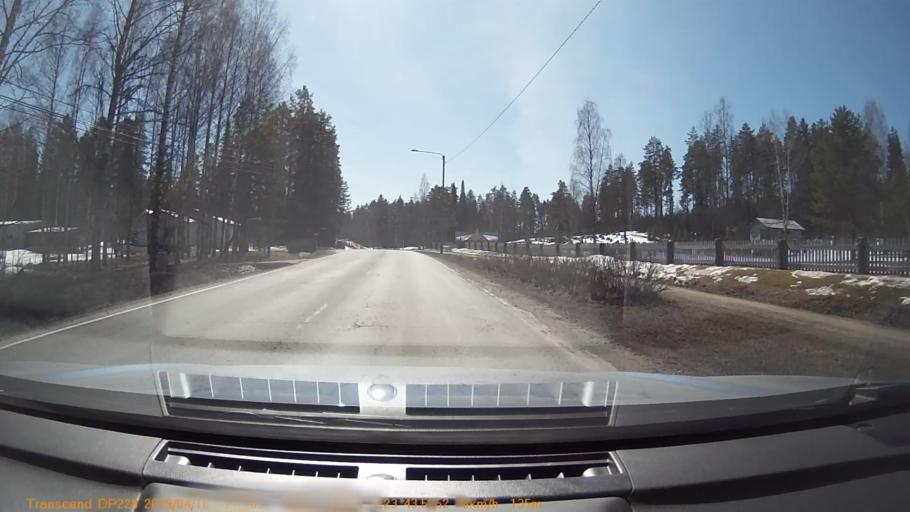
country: FI
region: Pirkanmaa
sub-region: Tampere
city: Kuru
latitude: 61.8658
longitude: 23.7259
